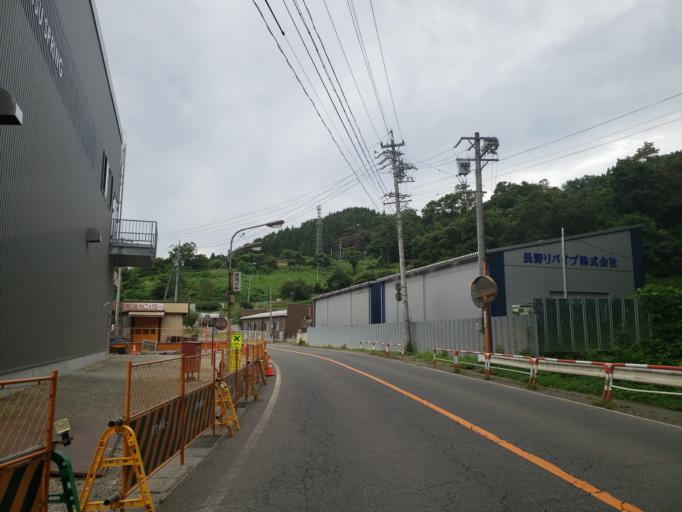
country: JP
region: Nagano
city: Nagano-shi
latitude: 36.6133
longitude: 138.0562
